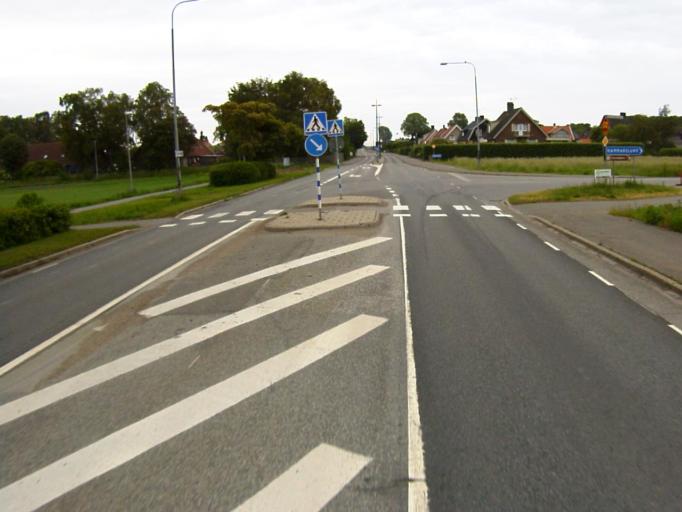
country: SE
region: Skane
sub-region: Kristianstads Kommun
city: Kristianstad
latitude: 56.0292
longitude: 14.1892
